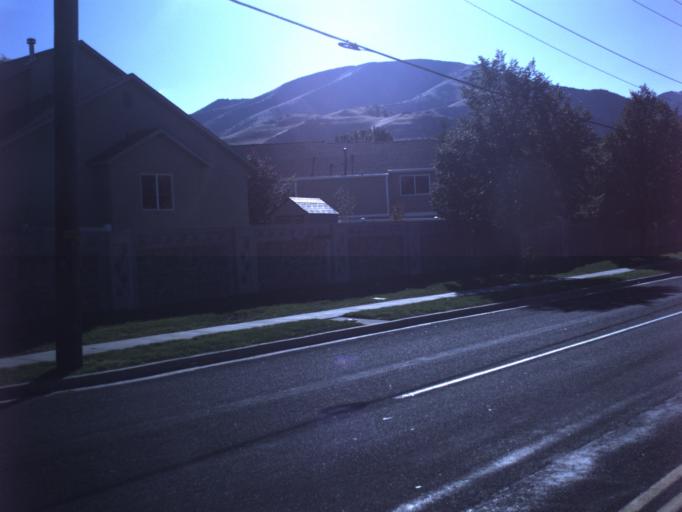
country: US
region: Utah
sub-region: Salt Lake County
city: Magna
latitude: 40.6965
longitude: -112.0942
